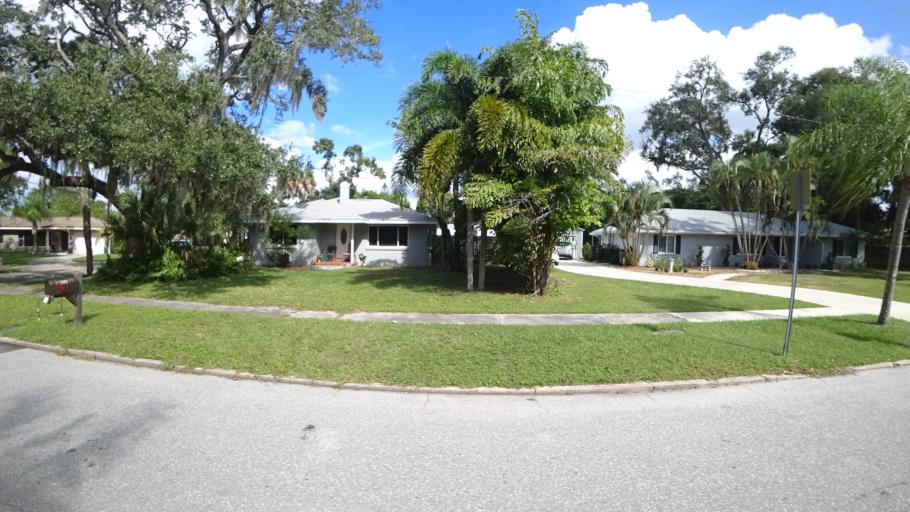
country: US
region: Florida
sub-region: Manatee County
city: Ellenton
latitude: 27.4988
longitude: -82.5395
